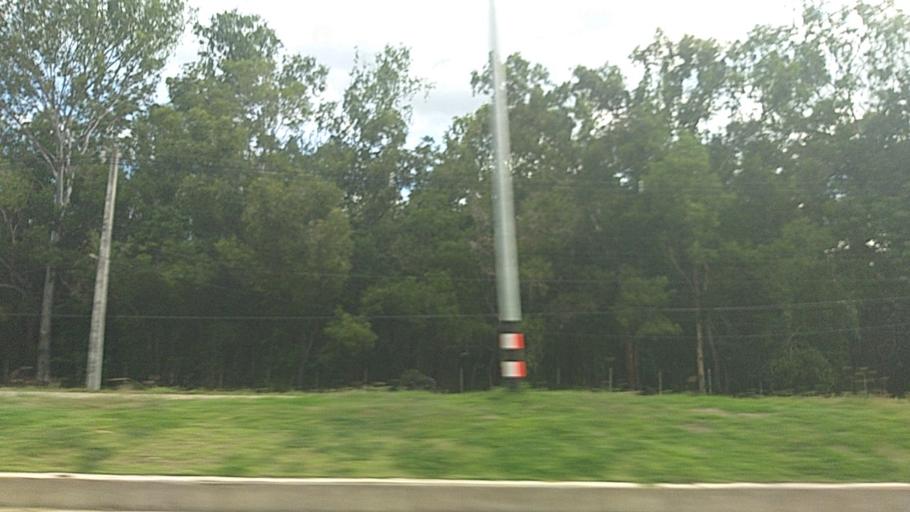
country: TH
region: Surin
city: Kap Choeng
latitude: 14.5486
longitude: 103.5115
